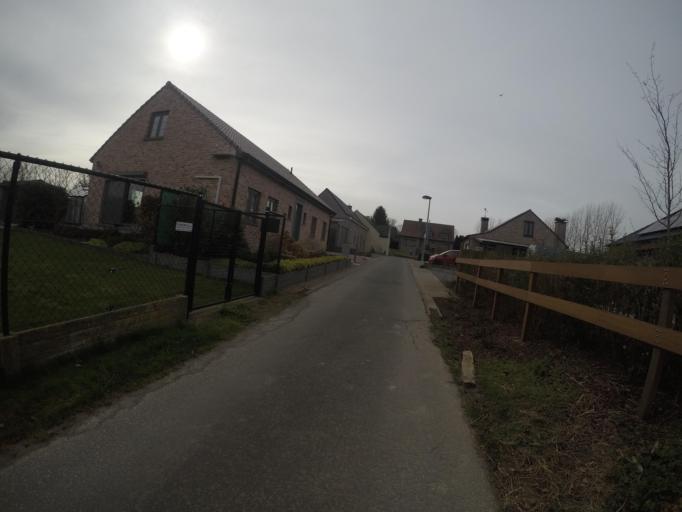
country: BE
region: Flanders
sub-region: Provincie Oost-Vlaanderen
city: Sint-Maria-Lierde
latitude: 50.8175
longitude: 3.8079
